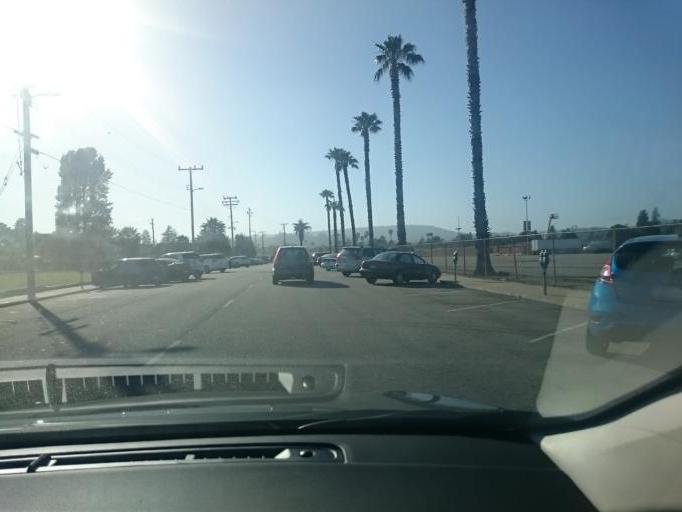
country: US
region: California
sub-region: Santa Cruz County
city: Twin Lakes
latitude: 36.9661
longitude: -122.0148
